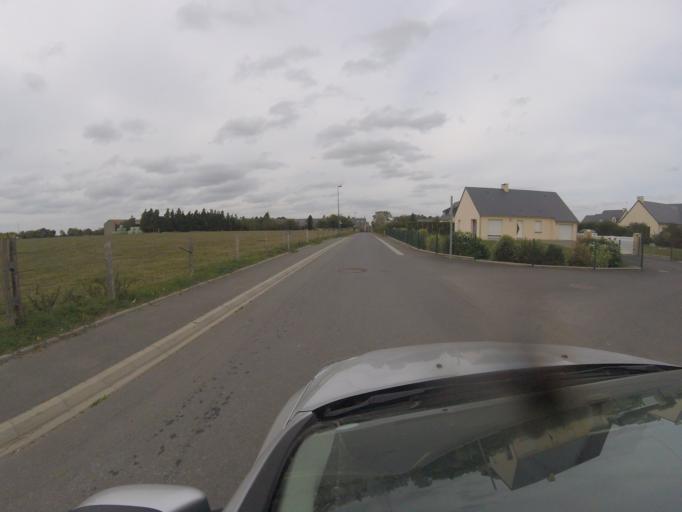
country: FR
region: Lower Normandy
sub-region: Departement de la Manche
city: Le Val-Saint-Pere
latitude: 48.6286
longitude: -1.3879
